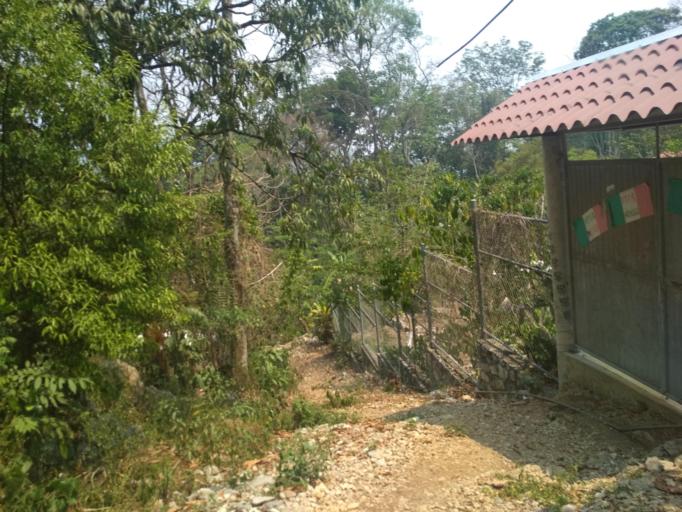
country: MX
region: Veracruz
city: Cosolapa
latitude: 18.5954
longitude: -96.7279
